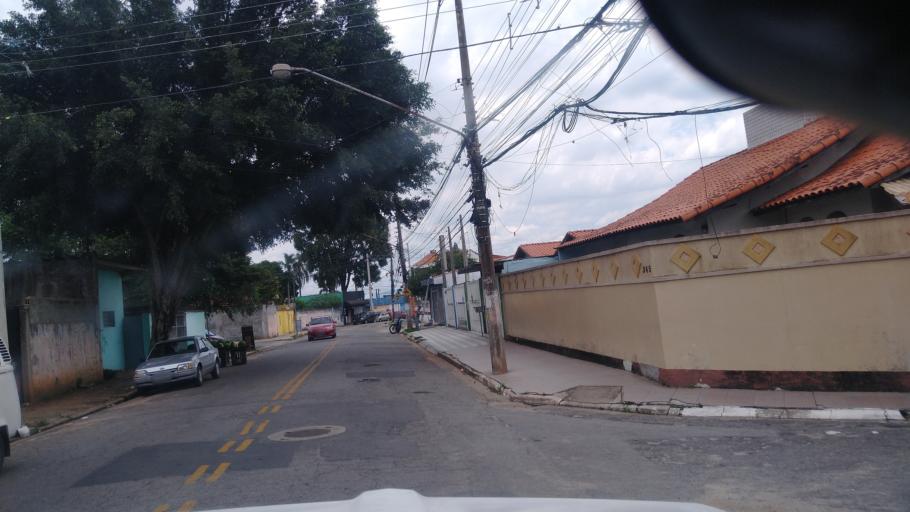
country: BR
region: Sao Paulo
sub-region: Suzano
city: Suzano
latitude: -23.5549
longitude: -46.3230
